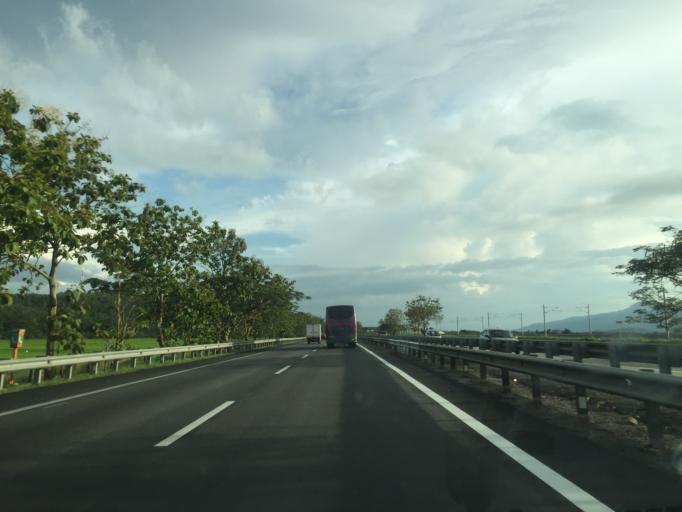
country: MY
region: Kedah
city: Gurun
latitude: 5.9131
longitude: 100.4694
